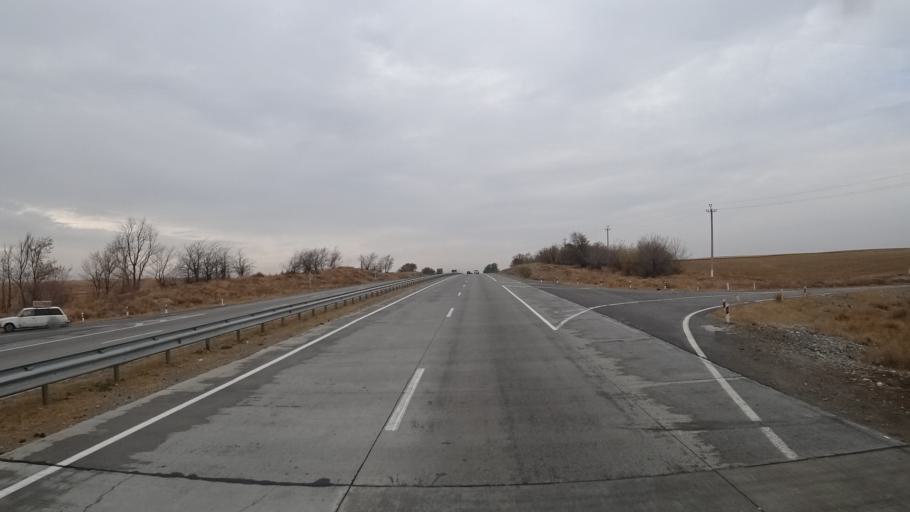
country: KZ
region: Ongtustik Qazaqstan
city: Aksu
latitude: 42.4779
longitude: 69.9102
